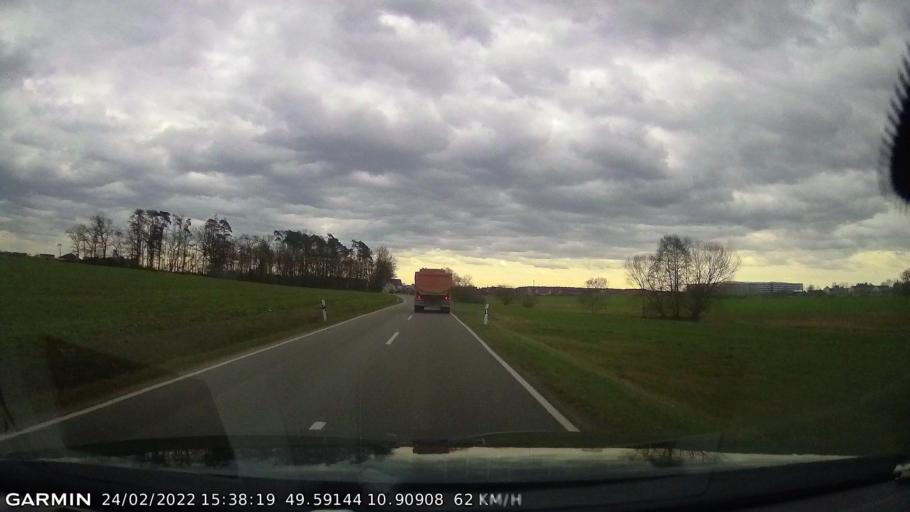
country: DE
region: Bavaria
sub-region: Regierungsbezirk Mittelfranken
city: Herzogenaurach
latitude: 49.5914
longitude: 10.9091
